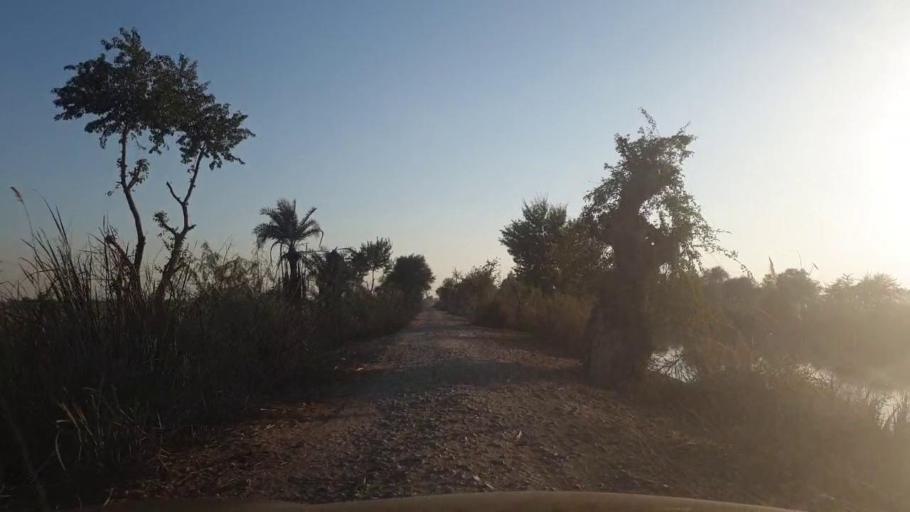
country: PK
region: Sindh
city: Mirpur Mathelo
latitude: 27.9960
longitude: 69.4667
